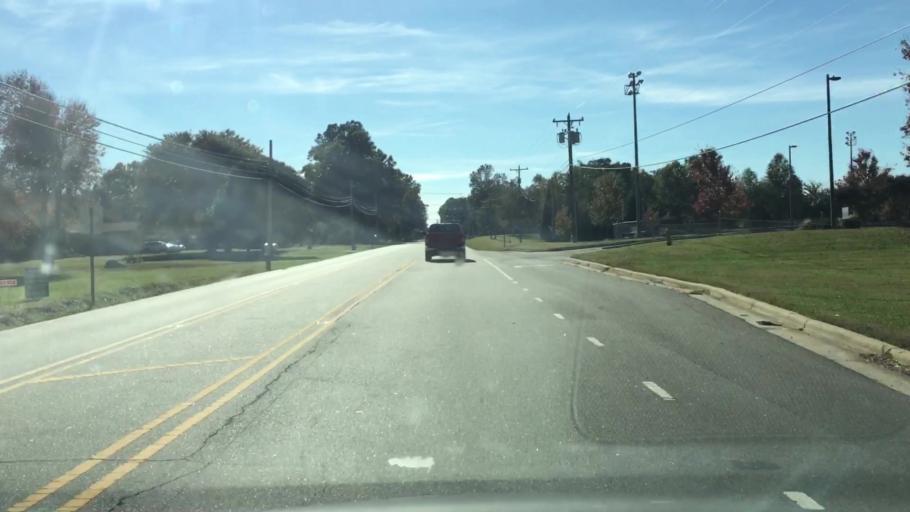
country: US
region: North Carolina
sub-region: Iredell County
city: Mooresville
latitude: 35.5958
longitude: -80.7833
